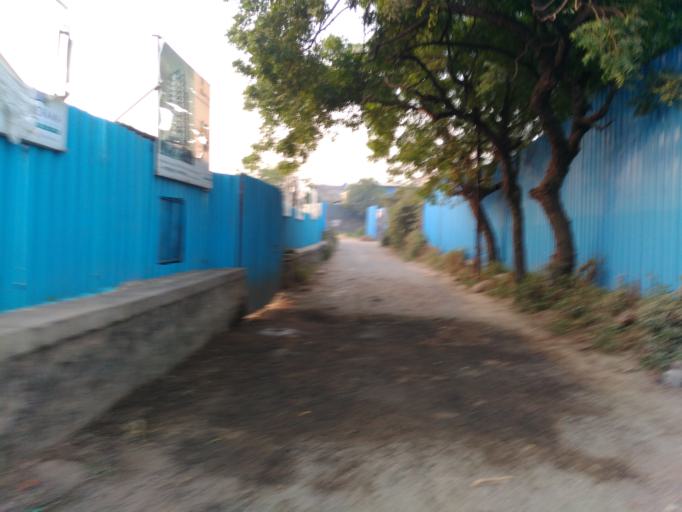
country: IN
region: Maharashtra
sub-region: Pune Division
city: Pune
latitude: 18.4566
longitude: 73.8948
